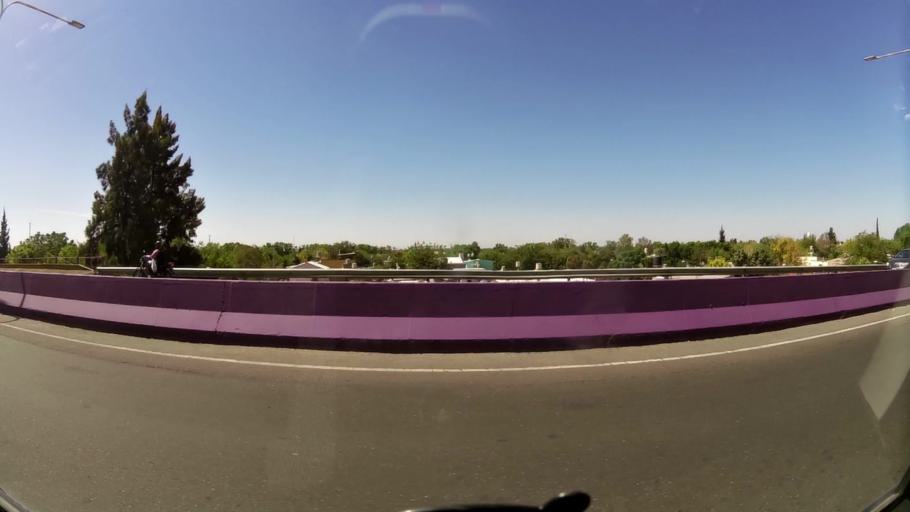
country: AR
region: Mendoza
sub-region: Departamento de Godoy Cruz
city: Godoy Cruz
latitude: -32.9292
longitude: -68.8642
